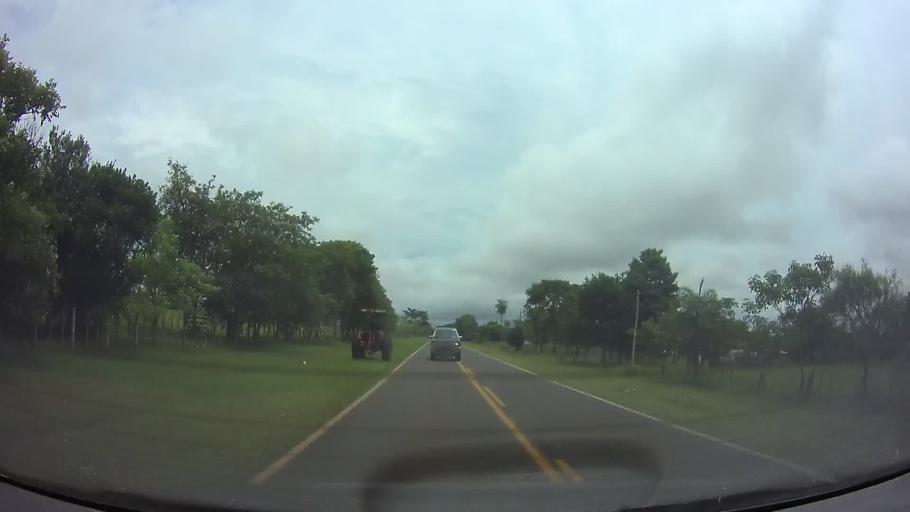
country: PY
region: Paraguari
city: Ybycui
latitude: -25.9817
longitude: -57.0701
